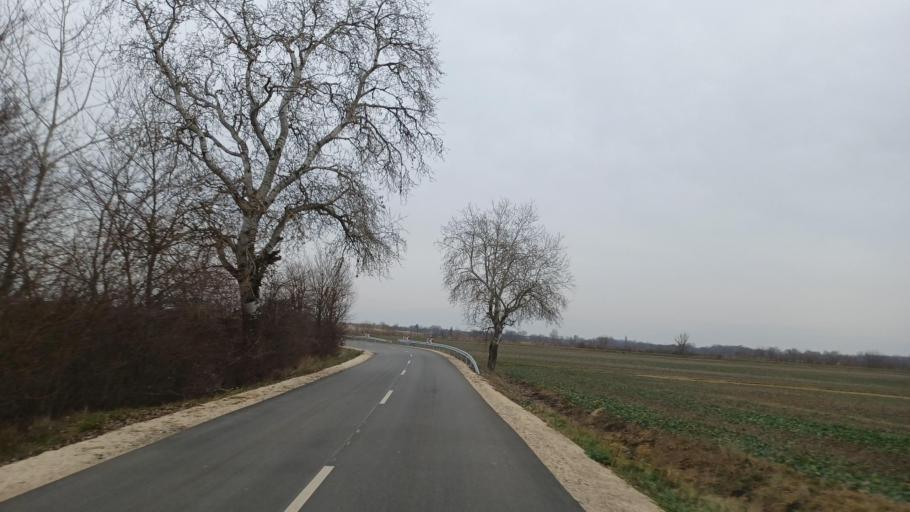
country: HU
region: Tolna
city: Nagydorog
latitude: 46.5615
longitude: 18.6009
